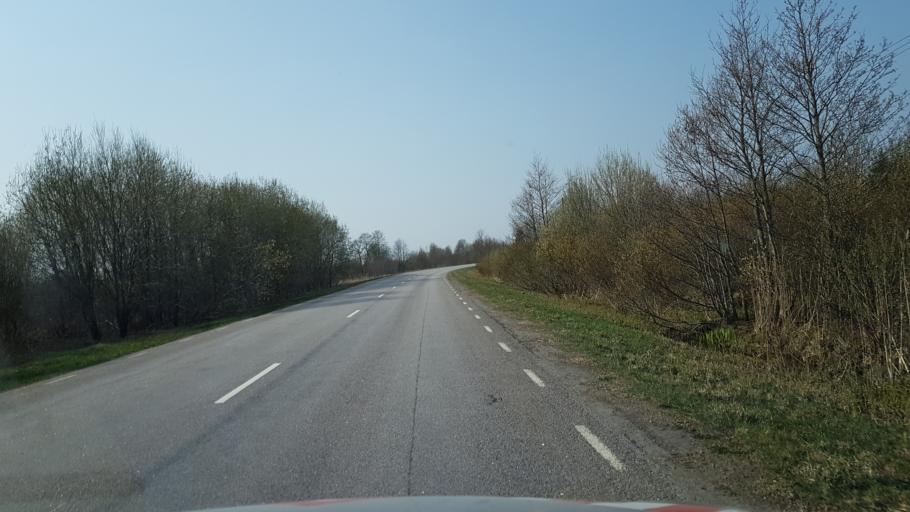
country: EE
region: Harju
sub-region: Paldiski linn
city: Paldiski
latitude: 59.3233
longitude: 24.1237
